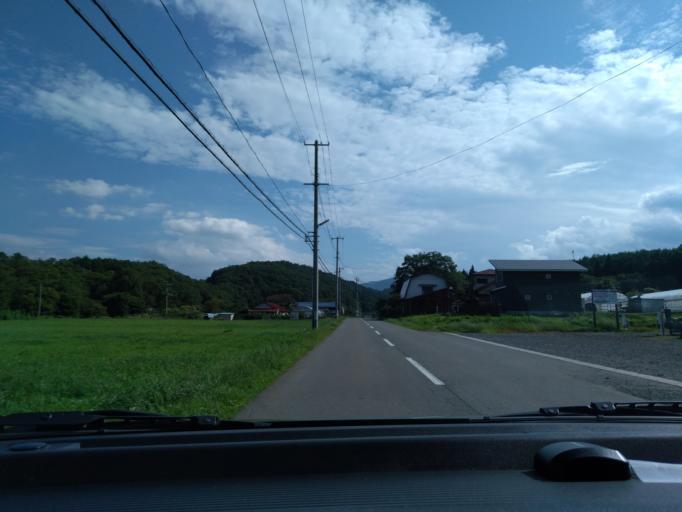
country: JP
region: Iwate
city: Shizukuishi
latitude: 39.6493
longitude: 140.9930
